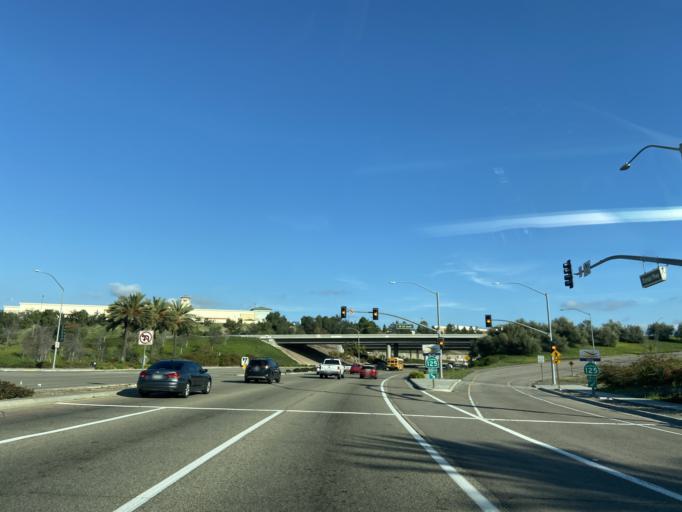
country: US
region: California
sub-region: San Diego County
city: Bonita
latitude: 32.6322
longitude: -116.9734
